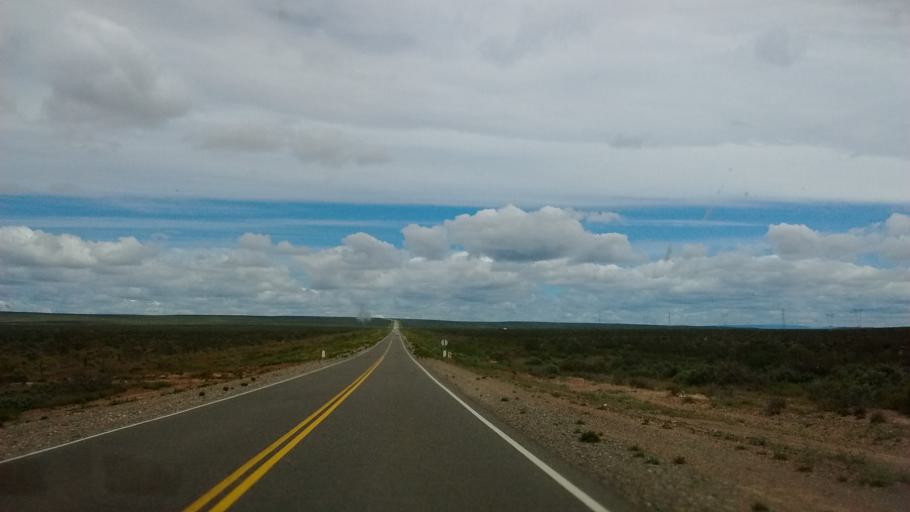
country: AR
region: Neuquen
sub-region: Departamento de Picun Leufu
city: Picun Leufu
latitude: -39.7127
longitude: -69.5169
